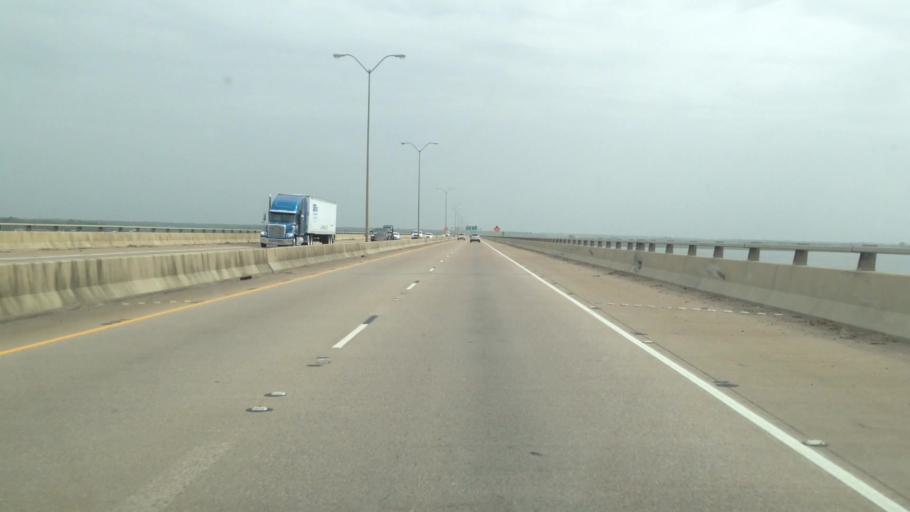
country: US
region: Louisiana
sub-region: Caddo Parish
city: Shreveport
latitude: 32.5005
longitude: -93.8185
